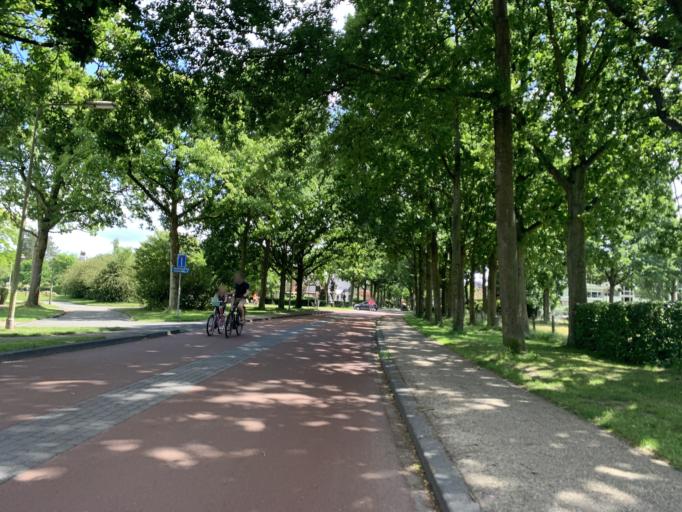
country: NL
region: Groningen
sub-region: Gemeente Haren
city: Haren
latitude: 53.1688
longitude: 6.6135
